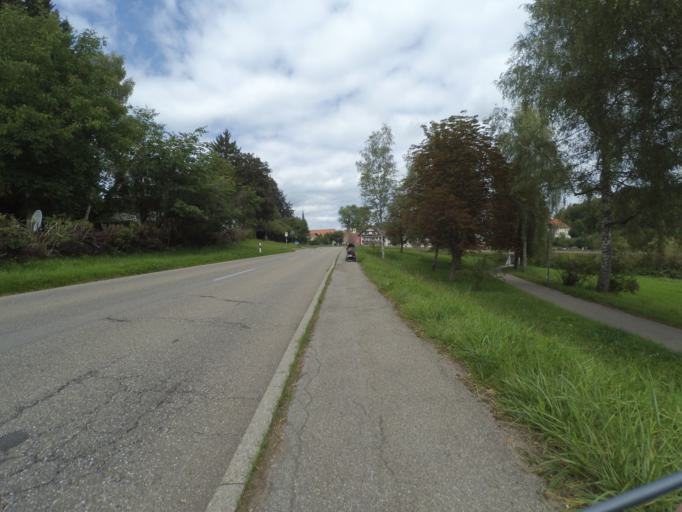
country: DE
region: Baden-Wuerttemberg
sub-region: Freiburg Region
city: Loffingen
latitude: 47.8793
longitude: 8.3464
